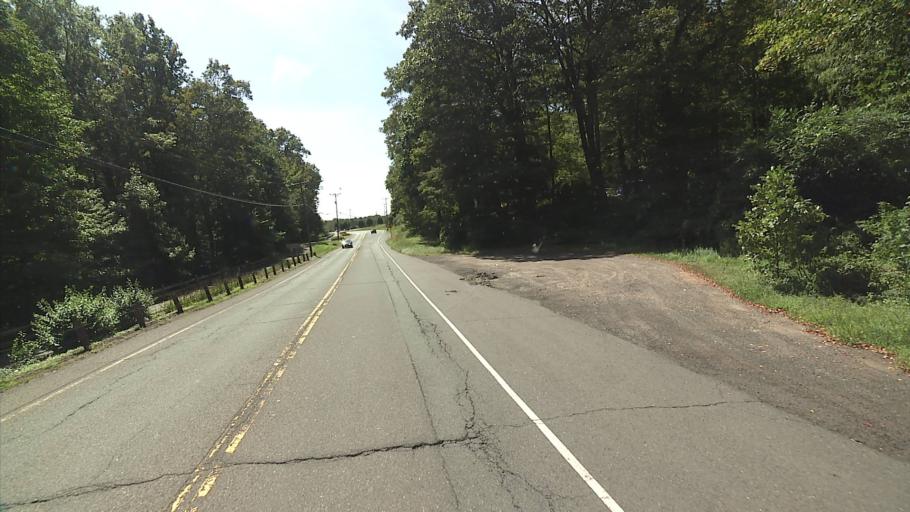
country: US
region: Connecticut
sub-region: New Haven County
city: Middlebury
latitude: 41.5241
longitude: -73.1336
